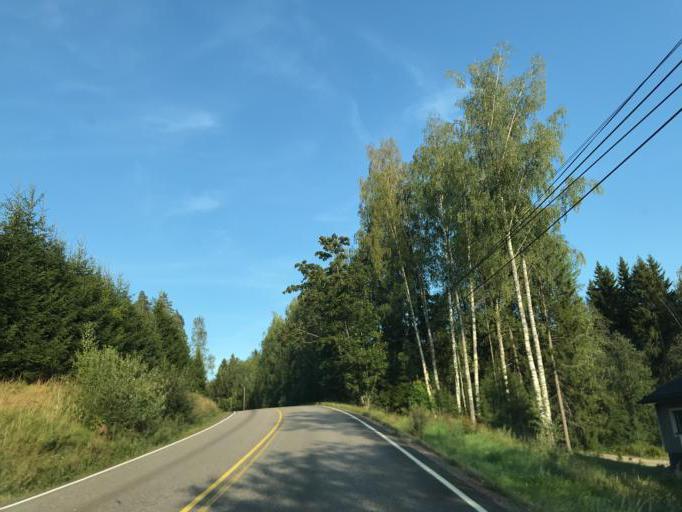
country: FI
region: Uusimaa
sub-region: Helsinki
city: Vihti
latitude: 60.4173
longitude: 24.4021
